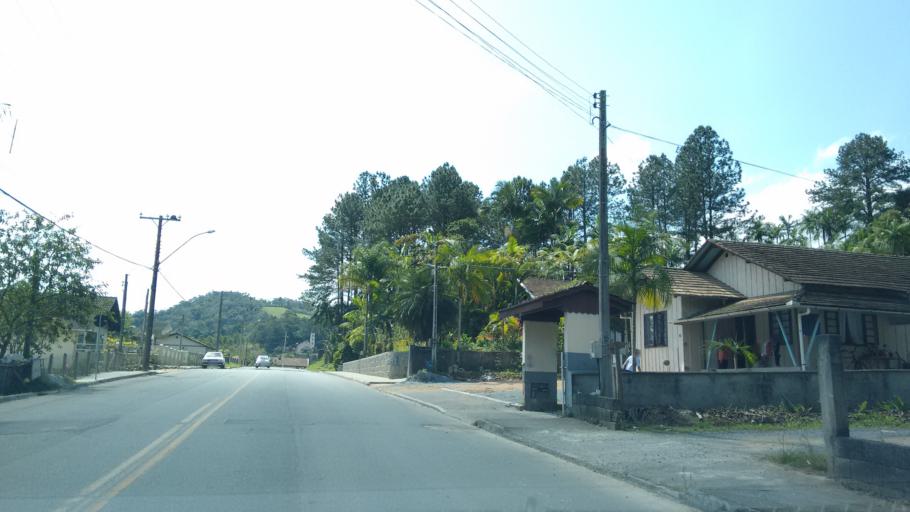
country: BR
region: Santa Catarina
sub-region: Pomerode
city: Pomerode
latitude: -26.7225
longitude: -49.1793
